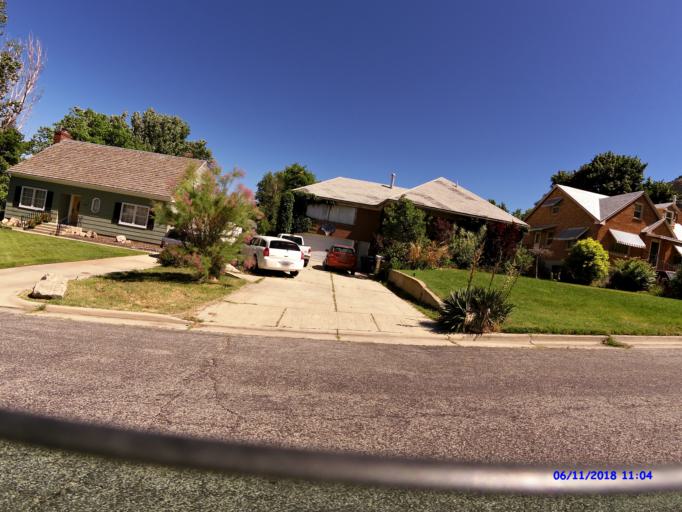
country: US
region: Utah
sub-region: Weber County
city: Ogden
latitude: 41.2180
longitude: -111.9339
